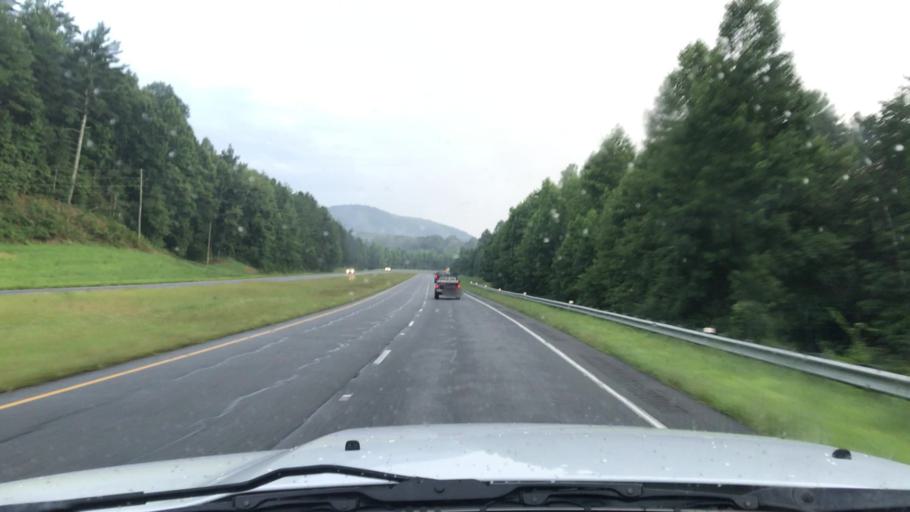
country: US
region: Georgia
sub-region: Gilmer County
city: Ellijay
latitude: 34.7661
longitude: -84.4013
